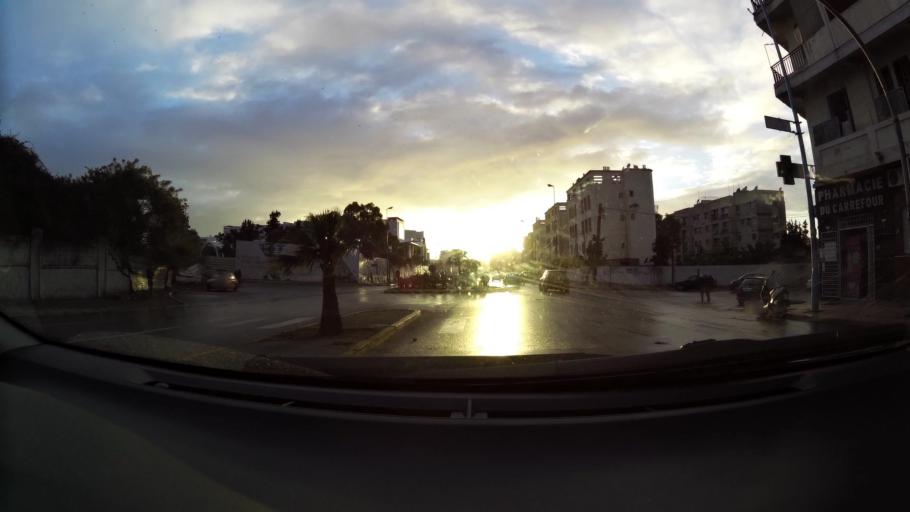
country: MA
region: Grand Casablanca
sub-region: Casablanca
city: Casablanca
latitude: 33.5868
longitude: -7.5902
